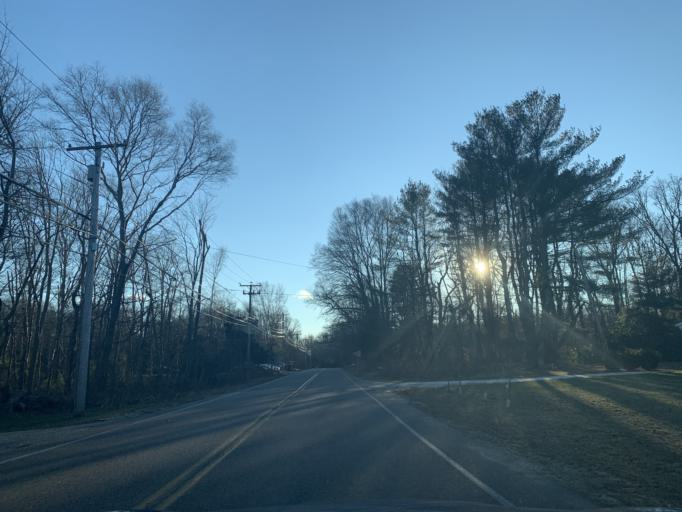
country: US
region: Massachusetts
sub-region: Bristol County
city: Rehoboth
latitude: 41.8730
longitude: -71.2314
